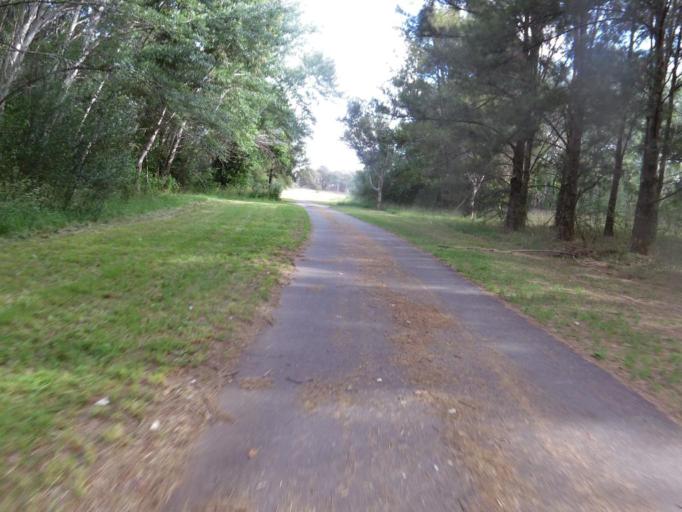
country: AU
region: Australian Capital Territory
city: Belconnen
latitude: -35.2203
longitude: 149.0805
